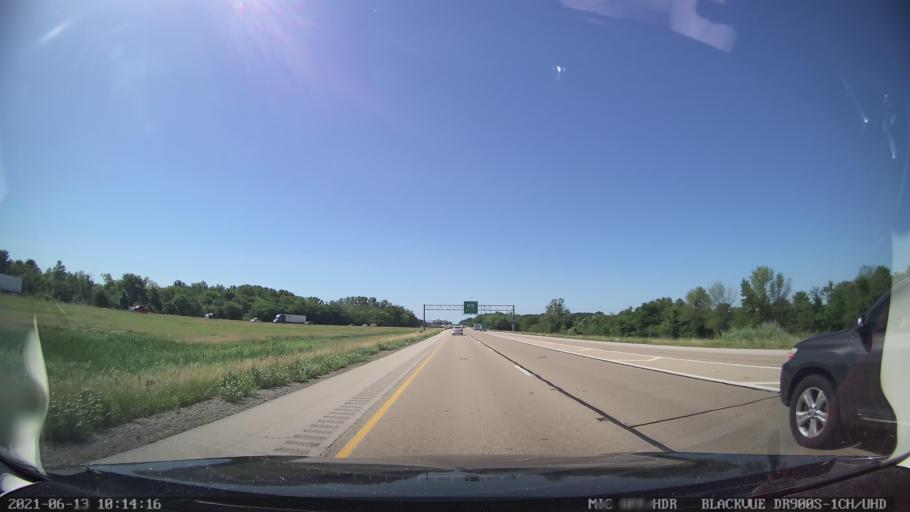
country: US
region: Illinois
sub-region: Logan County
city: Lincoln
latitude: 40.1726
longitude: -89.4177
